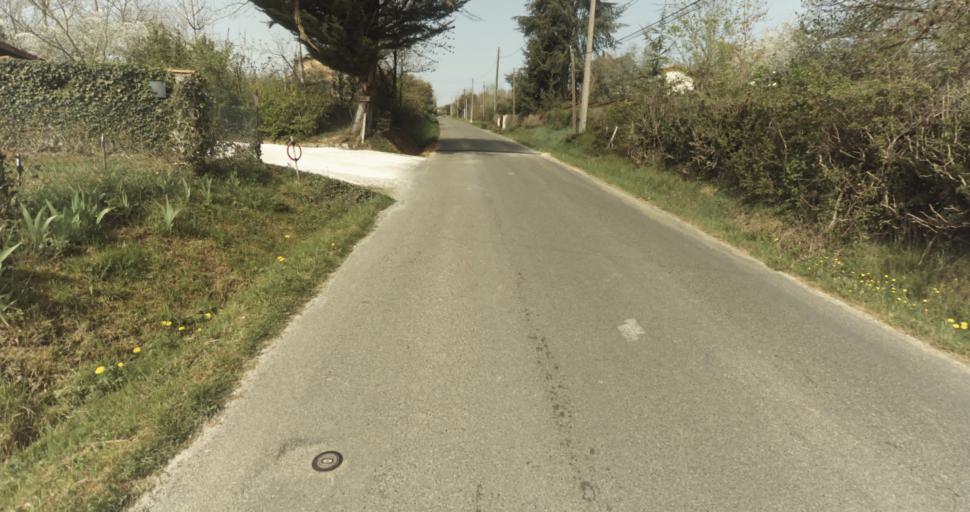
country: FR
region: Midi-Pyrenees
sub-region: Departement du Tarn-et-Garonne
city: Moissac
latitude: 44.1188
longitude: 1.0998
